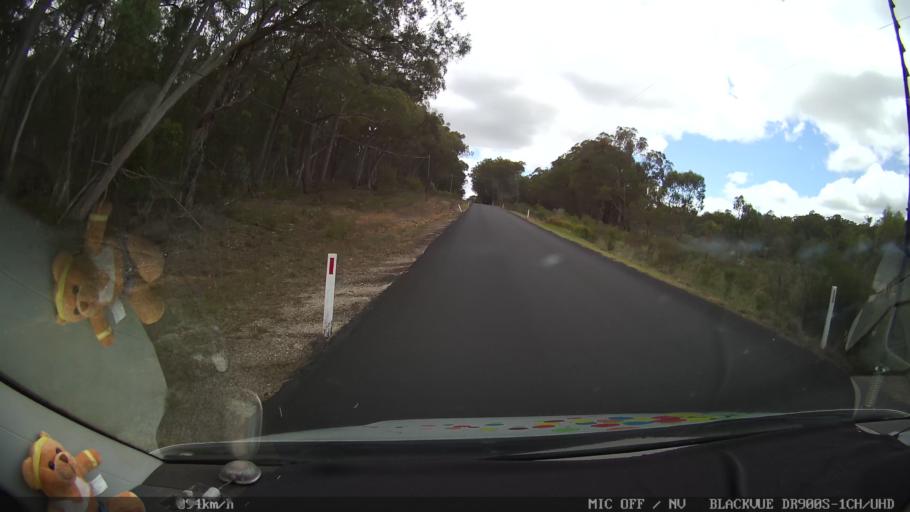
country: AU
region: New South Wales
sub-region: Glen Innes Severn
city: Glen Innes
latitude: -29.4370
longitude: 151.6295
